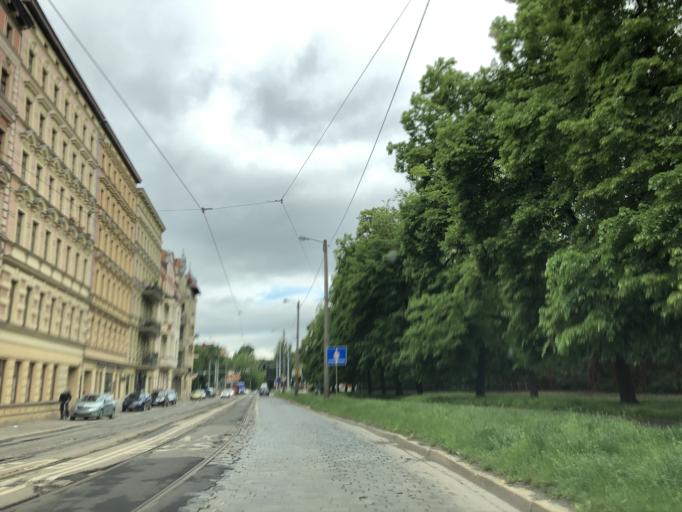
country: PL
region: Lower Silesian Voivodeship
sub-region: Powiat wroclawski
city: Wroclaw
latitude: 51.1242
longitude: 17.0293
